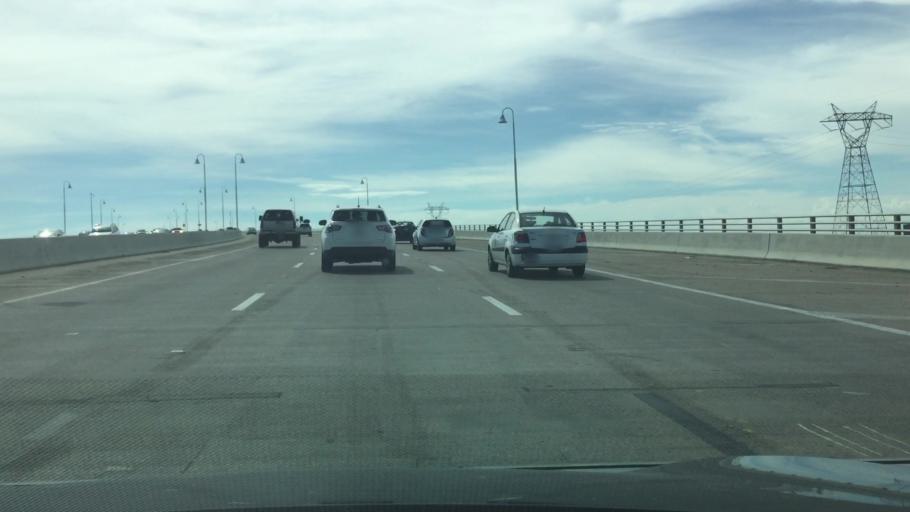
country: US
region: Florida
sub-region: Bay County
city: Upper Grand Lagoon
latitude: 30.1879
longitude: -85.7363
